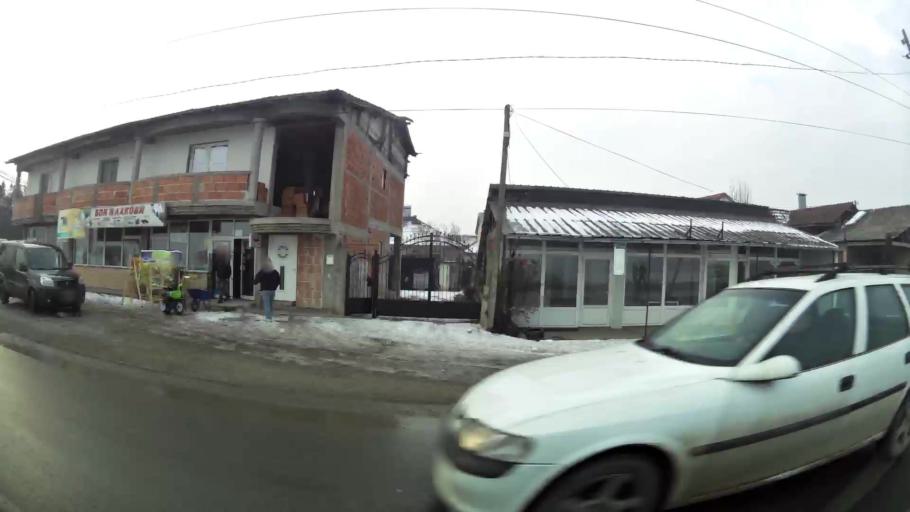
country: MK
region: Ilinden
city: Jurumleri
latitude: 41.9792
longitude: 21.5299
